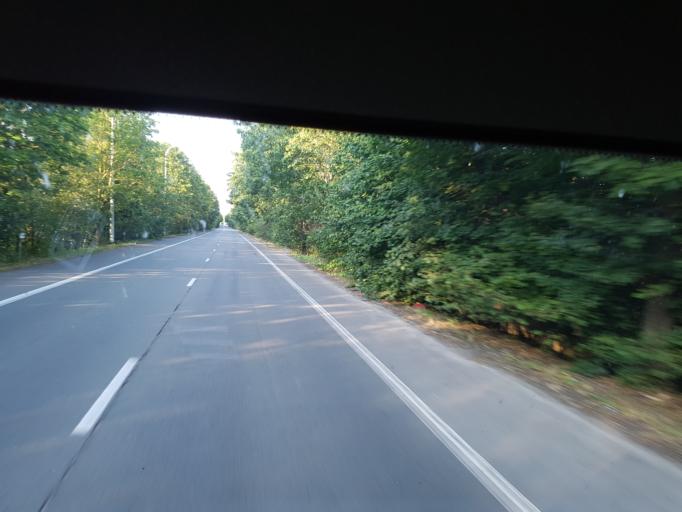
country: BE
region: Wallonia
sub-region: Province du Hainaut
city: Antoing
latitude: 50.5537
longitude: 3.4428
